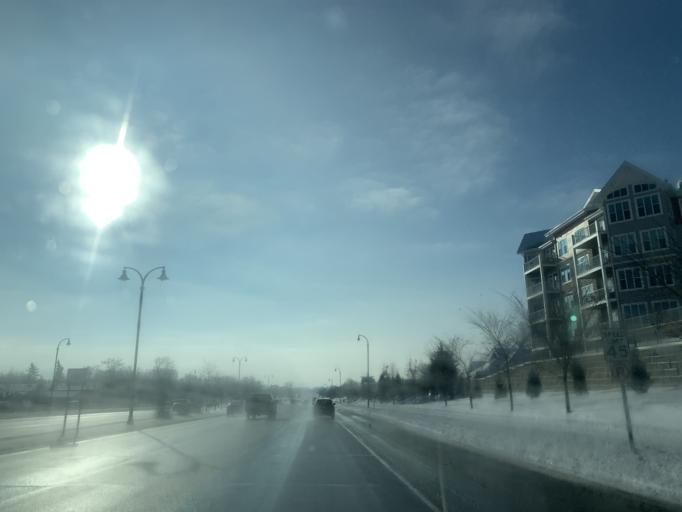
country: US
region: Minnesota
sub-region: Dakota County
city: Apple Valley
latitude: 44.7457
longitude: -93.2179
